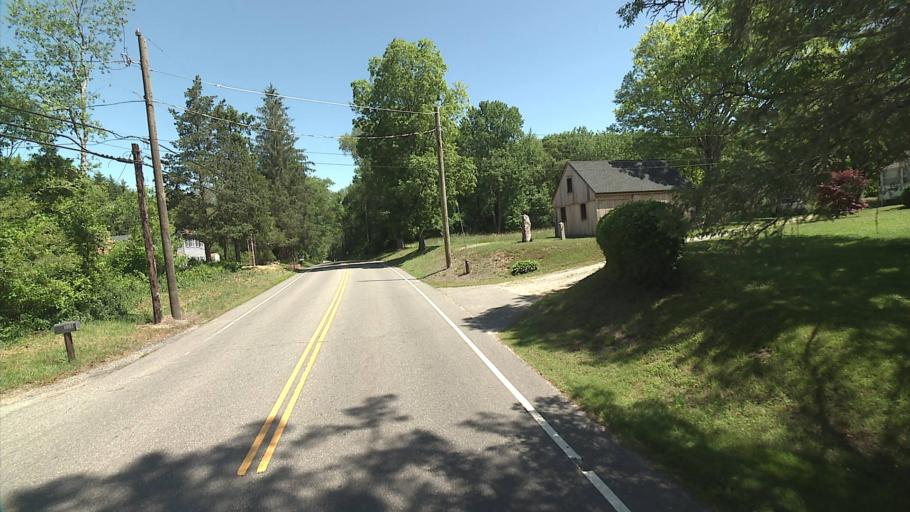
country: US
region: Rhode Island
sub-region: Washington County
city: Hopkinton
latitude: 41.4706
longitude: -71.8324
